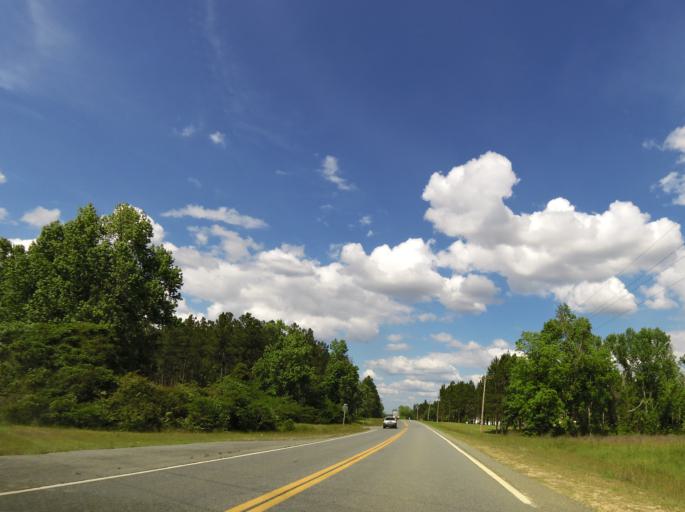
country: US
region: Georgia
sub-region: Treutlen County
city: Soperton
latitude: 32.3355
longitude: -82.6595
